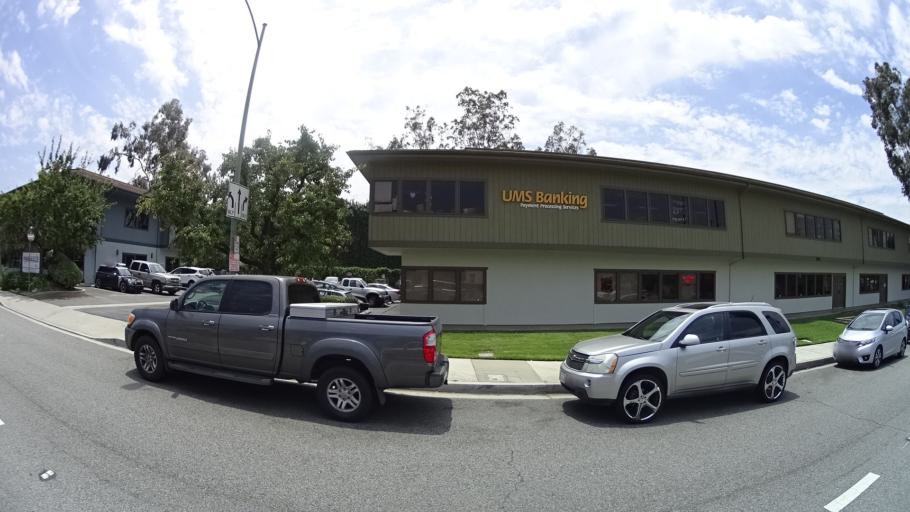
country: US
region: California
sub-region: Los Angeles County
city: North Glendale
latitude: 34.1556
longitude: -118.2722
